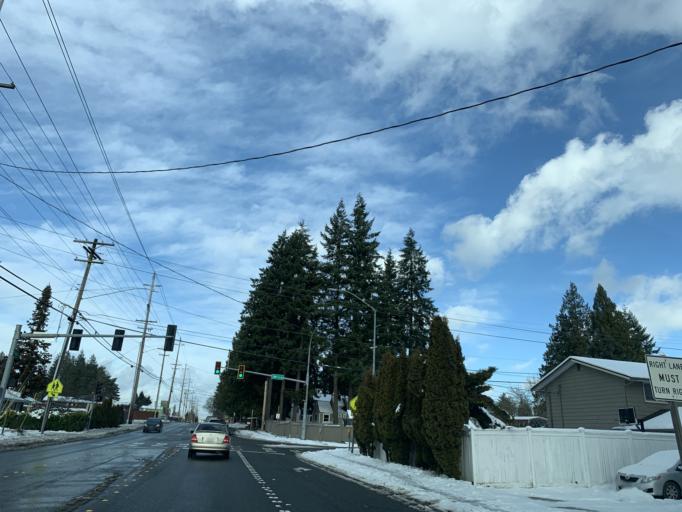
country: US
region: Washington
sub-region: Snohomish County
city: Martha Lake
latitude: 47.8996
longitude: -122.2389
